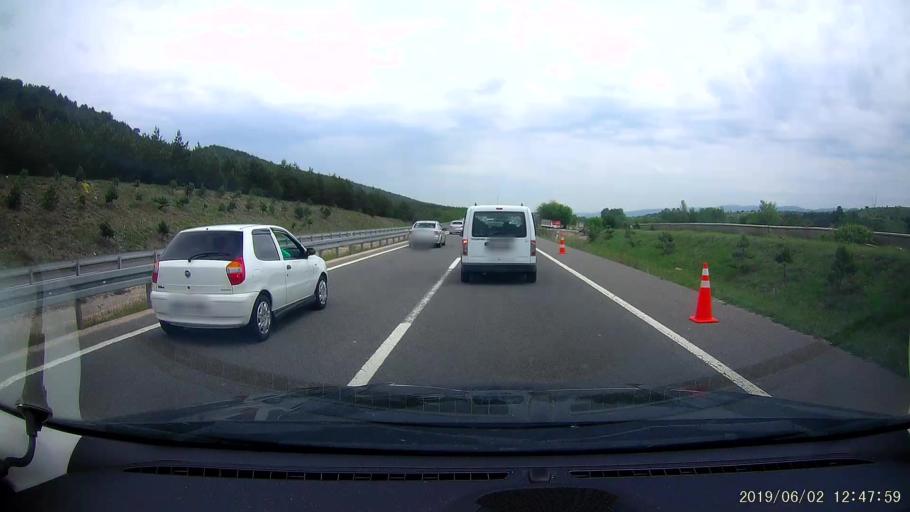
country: TR
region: Bolu
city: Gerede
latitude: 40.8237
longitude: 32.3265
